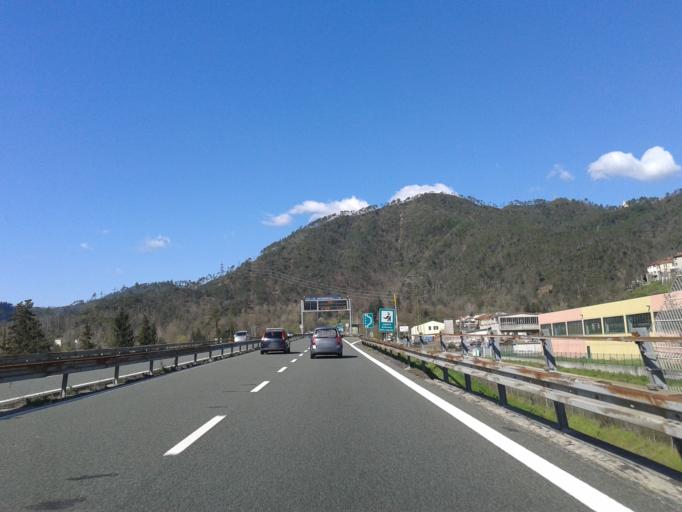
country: IT
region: Liguria
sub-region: Provincia di La Spezia
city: Beverino
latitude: 44.2056
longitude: 9.7933
